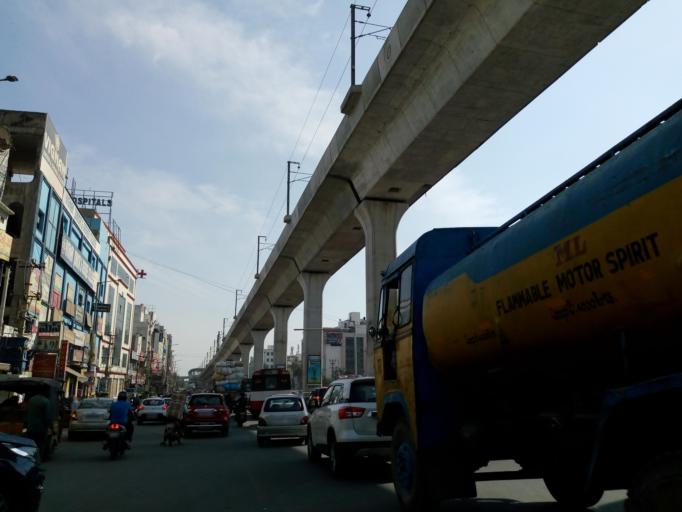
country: IN
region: Telangana
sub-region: Rangareddi
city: Uppal Kalan
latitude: 17.4191
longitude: 78.5416
